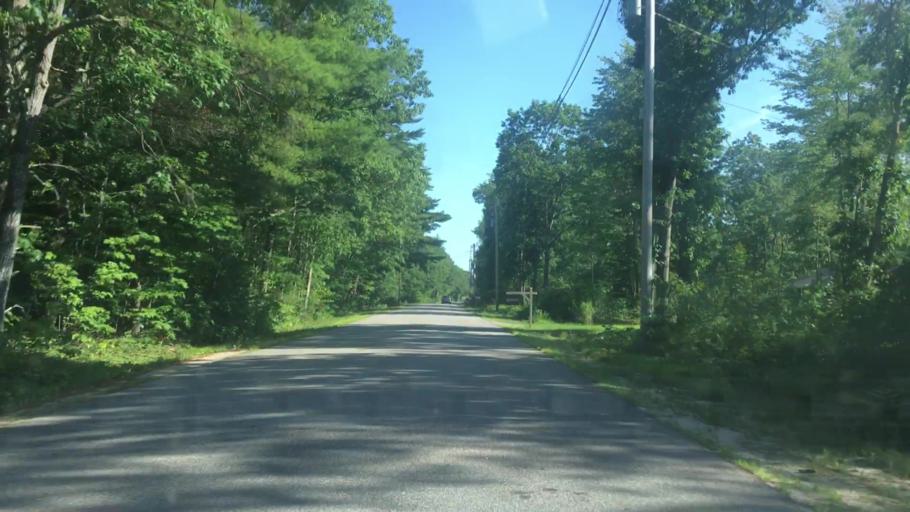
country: US
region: Maine
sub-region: Cumberland County
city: Gorham
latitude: 43.7336
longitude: -70.5167
